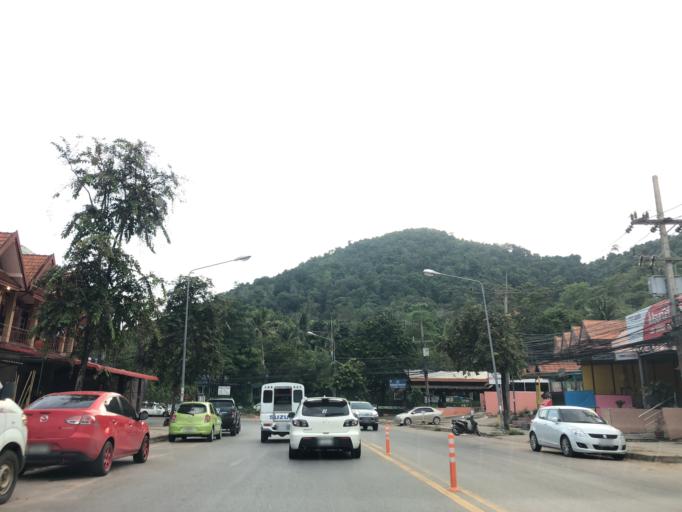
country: TH
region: Phangnga
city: Ban Ao Nang
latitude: 8.0389
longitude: 98.8339
